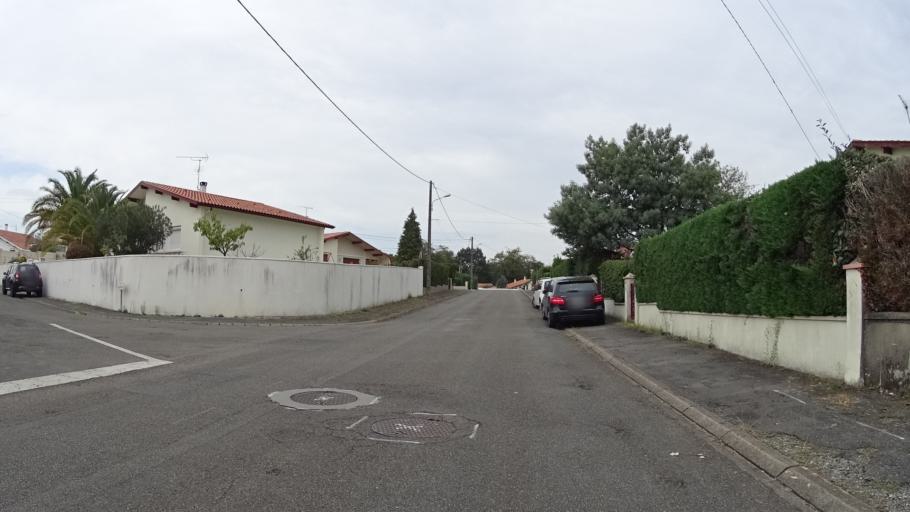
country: FR
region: Aquitaine
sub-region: Departement des Landes
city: Saint-Paul-les-Dax
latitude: 43.7288
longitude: -1.0727
